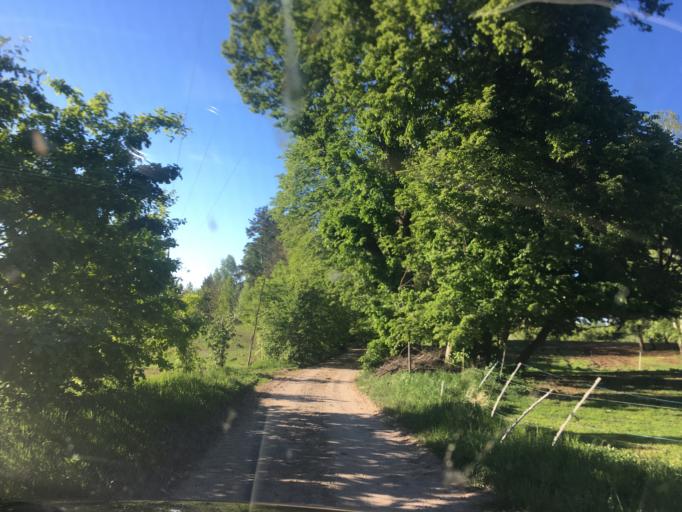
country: PL
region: Warmian-Masurian Voivodeship
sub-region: Powiat piski
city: Ruciane-Nida
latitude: 53.6561
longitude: 21.4834
